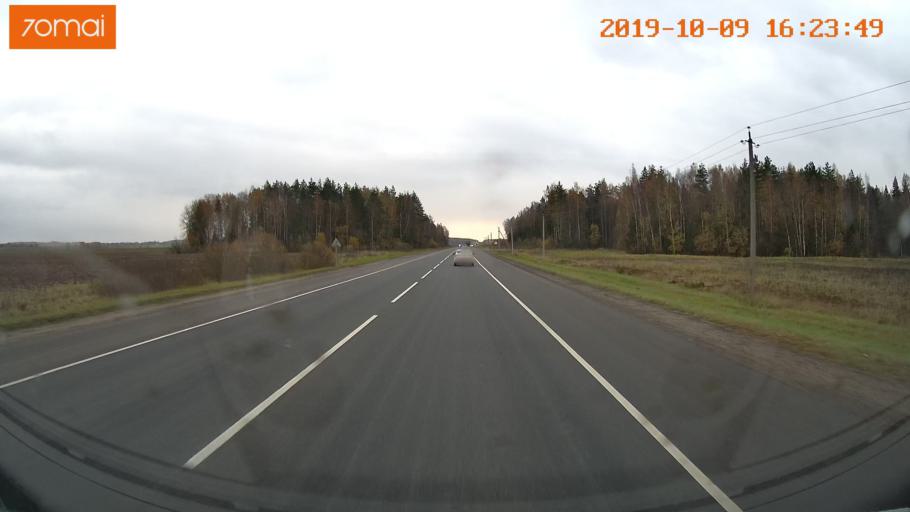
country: RU
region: Kostroma
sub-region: Kostromskoy Rayon
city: Kostroma
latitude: 57.6592
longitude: 40.9041
